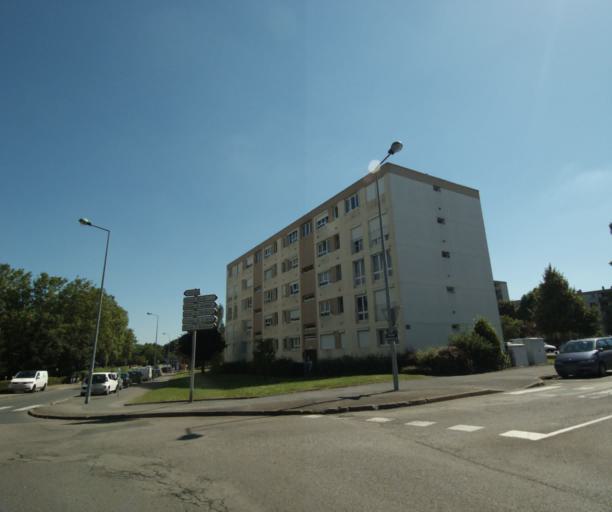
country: FR
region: Pays de la Loire
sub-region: Departement de la Mayenne
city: Laval
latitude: 48.0632
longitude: -0.7524
